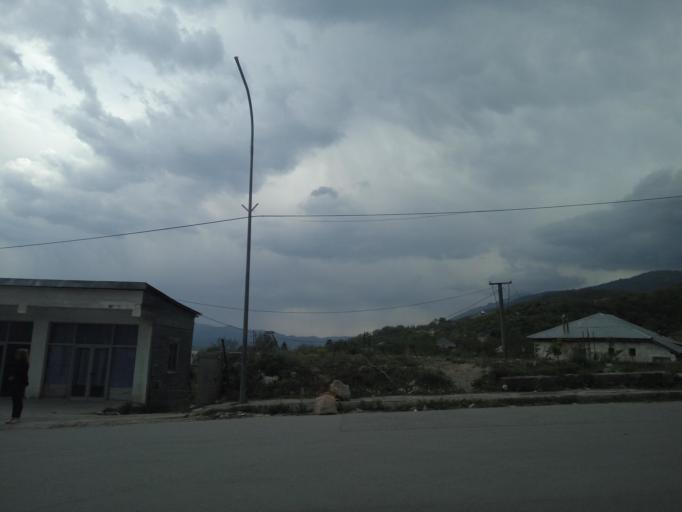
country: AL
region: Kukes
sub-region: Rrethi i Tropojes
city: Bajram Curri
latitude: 42.3561
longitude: 20.0771
